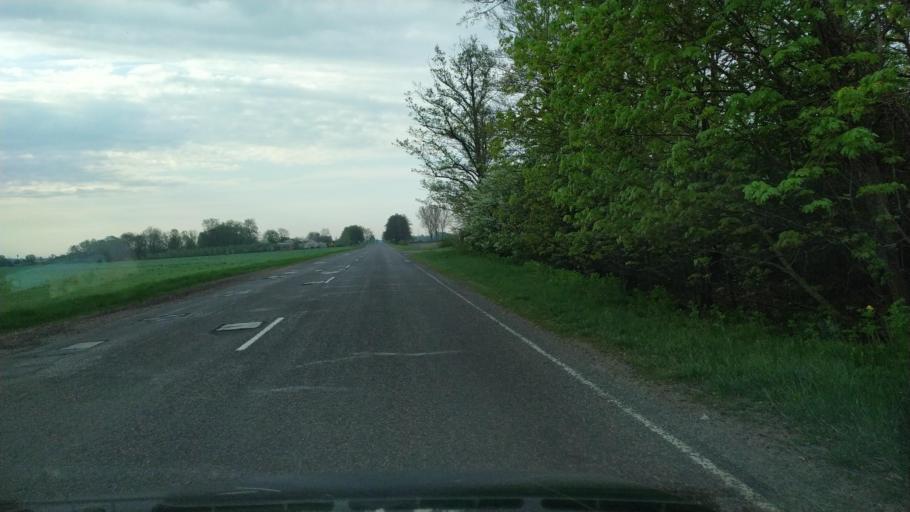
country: BY
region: Brest
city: Zhabinka
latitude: 52.2340
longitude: 23.9834
